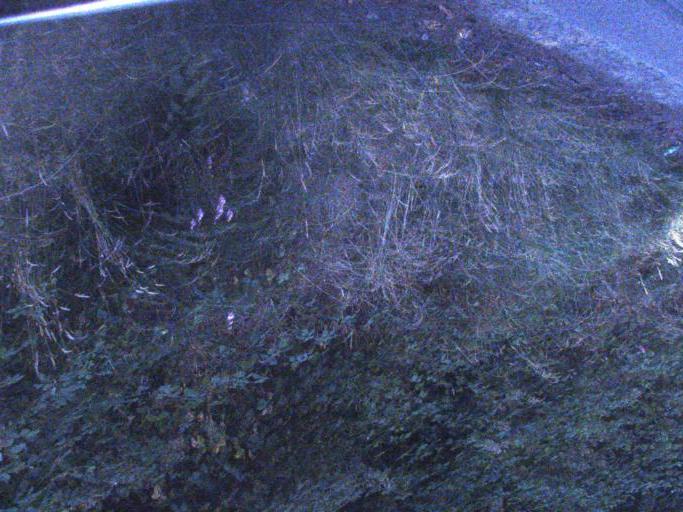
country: US
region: Washington
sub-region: King County
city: Enumclaw
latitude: 47.1679
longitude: -121.9126
